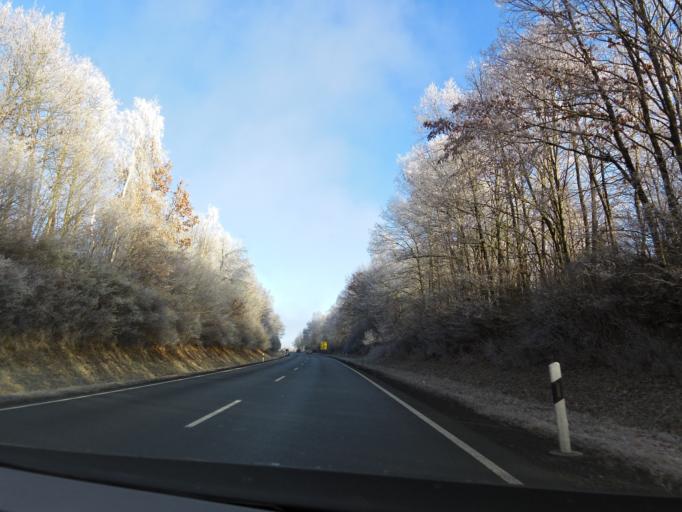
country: DE
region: Bavaria
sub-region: Upper Franconia
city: Arzberg
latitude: 50.0287
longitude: 12.1495
